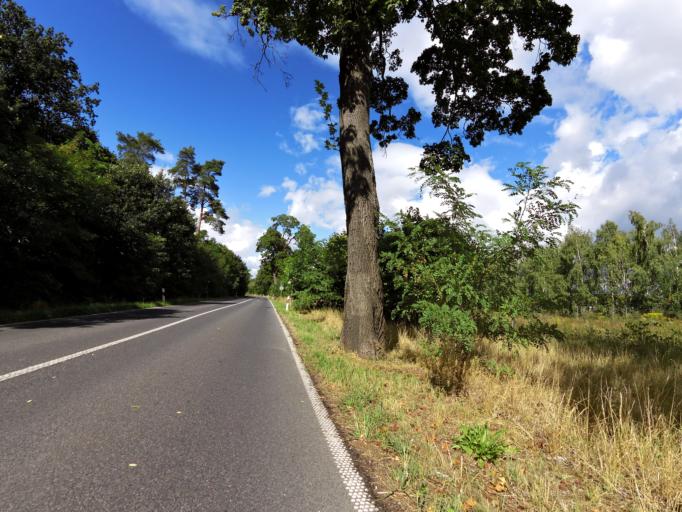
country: DE
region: Berlin
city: Marienfelde
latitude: 52.3692
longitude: 13.3616
